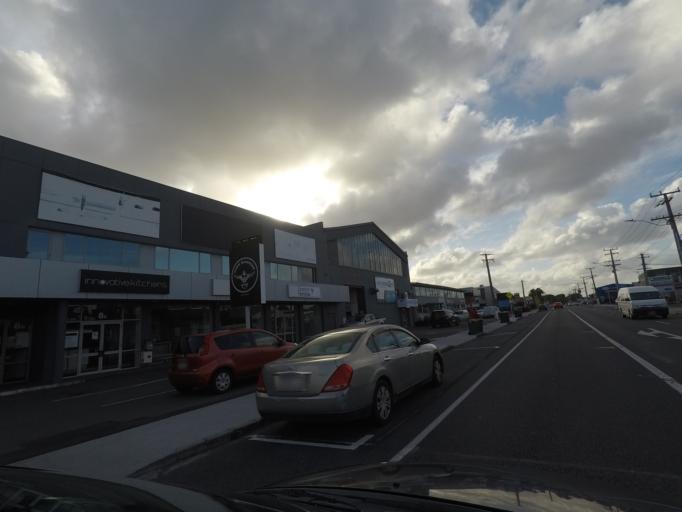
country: NZ
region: Auckland
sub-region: Auckland
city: Auckland
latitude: -36.9142
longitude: 174.7538
